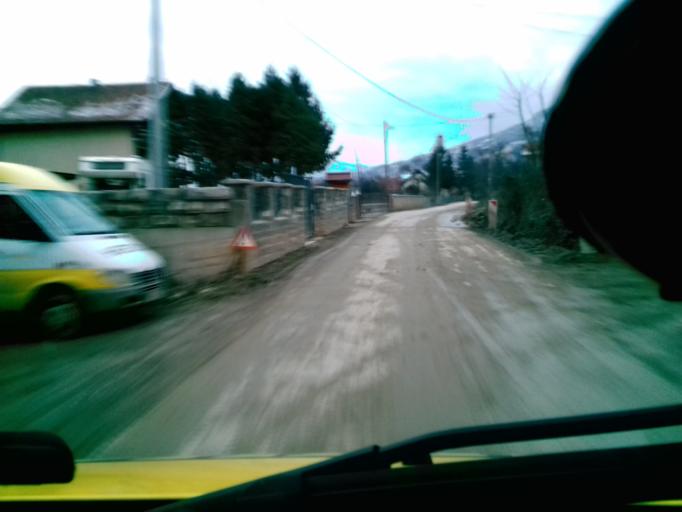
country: BA
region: Federation of Bosnia and Herzegovina
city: Zenica
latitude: 44.1812
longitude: 17.9727
